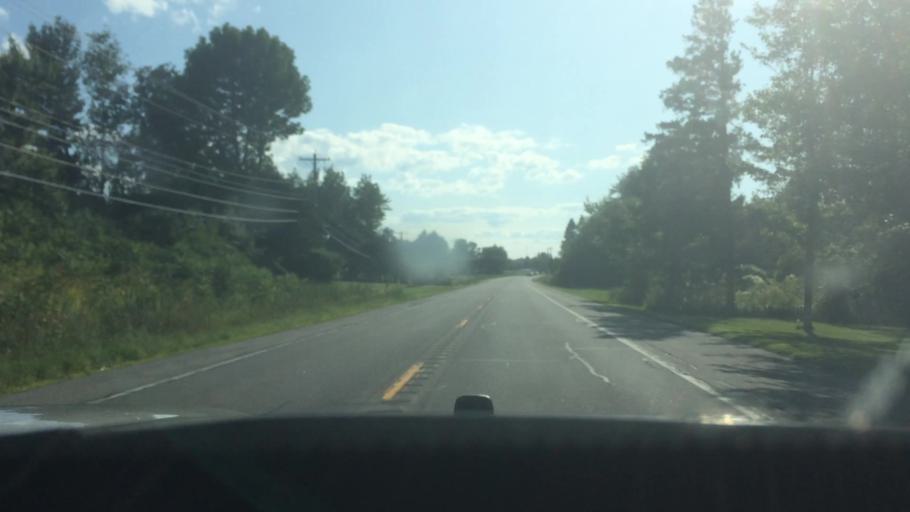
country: US
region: New York
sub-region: Franklin County
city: Malone
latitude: 44.8325
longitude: -74.3282
